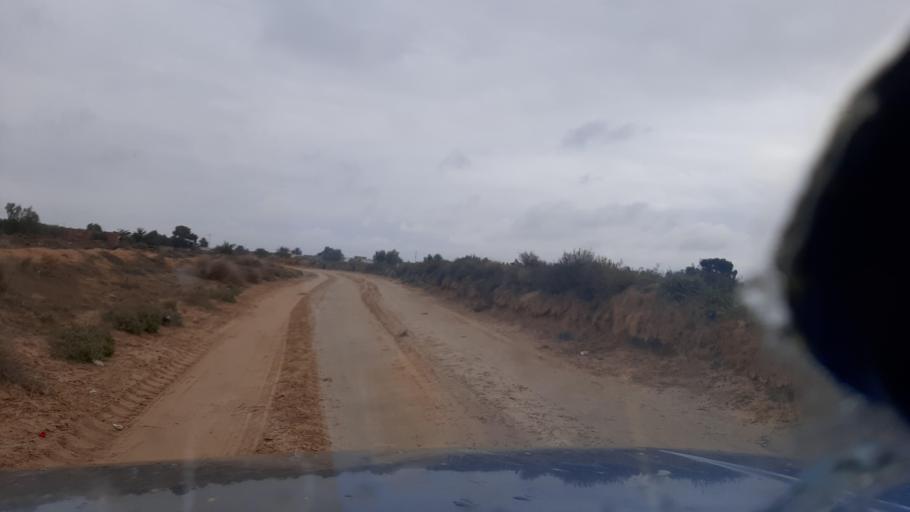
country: TN
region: Al Mahdiyah
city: Shurban
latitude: 35.4356
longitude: 10.4012
